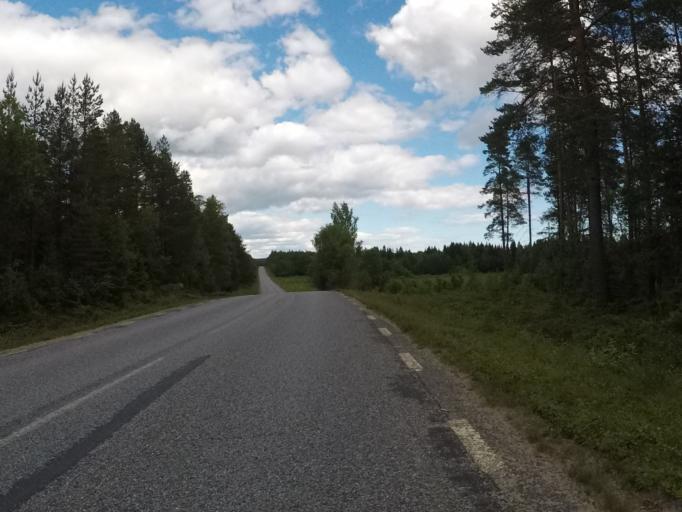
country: SE
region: Vaesterbotten
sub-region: Umea Kommun
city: Saevar
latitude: 63.9395
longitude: 20.7865
